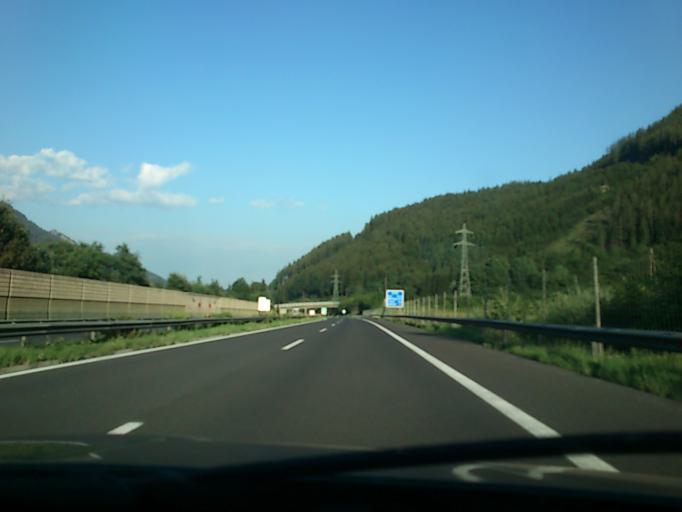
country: AT
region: Styria
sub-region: Politischer Bezirk Leoben
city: Mautern in Steiermark
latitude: 47.3953
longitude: 14.8266
